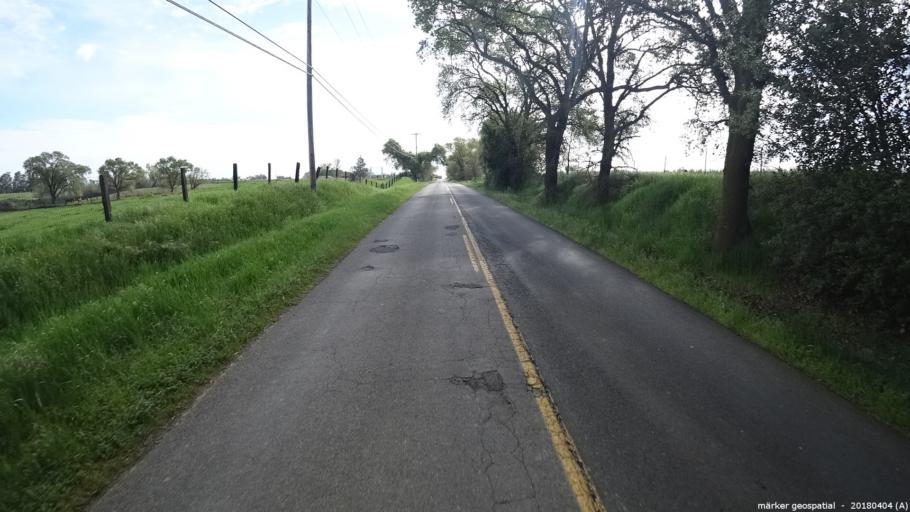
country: US
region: California
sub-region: Sacramento County
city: Herald
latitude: 38.2553
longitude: -121.2532
